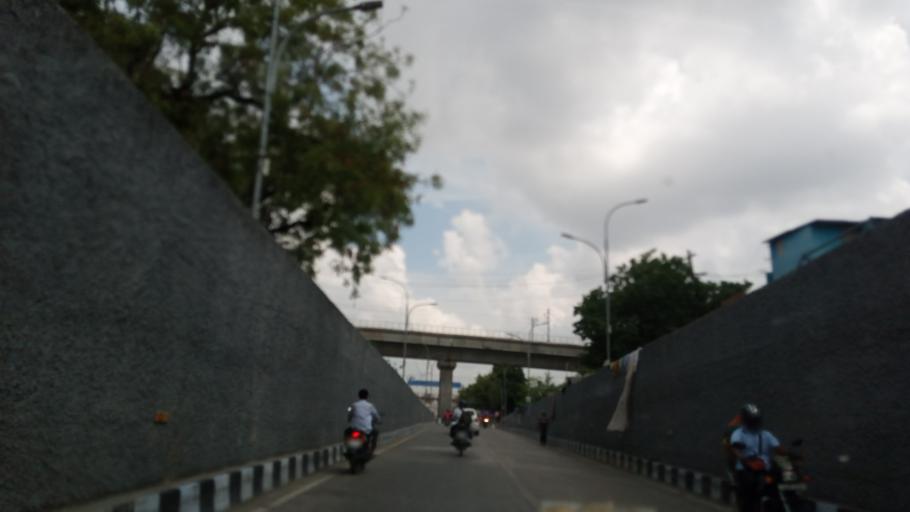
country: IN
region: Tamil Nadu
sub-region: Kancheepuram
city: Manappakkam
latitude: 12.9863
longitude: 80.1764
